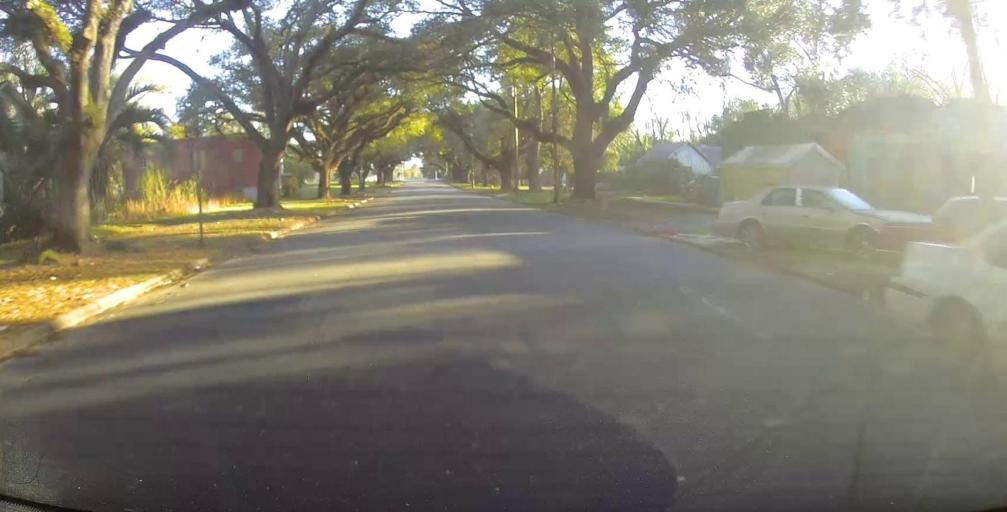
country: US
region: Georgia
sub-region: Dougherty County
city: Albany
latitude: 31.5690
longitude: -84.1590
